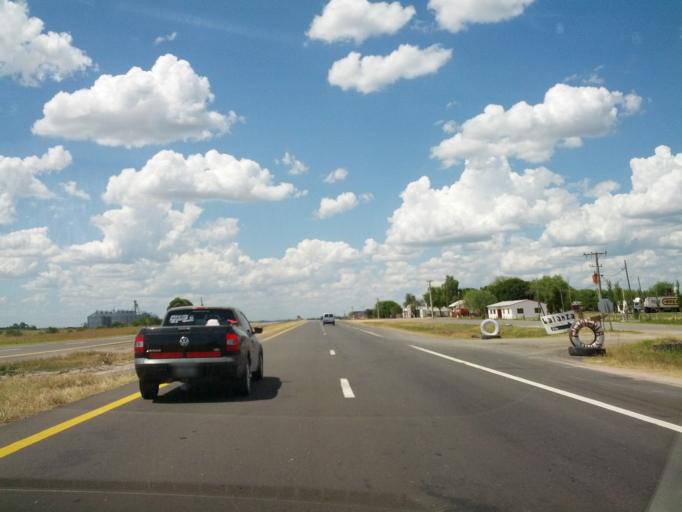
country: AR
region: Entre Rios
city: Colonia Elia
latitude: -32.5511
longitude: -58.3569
